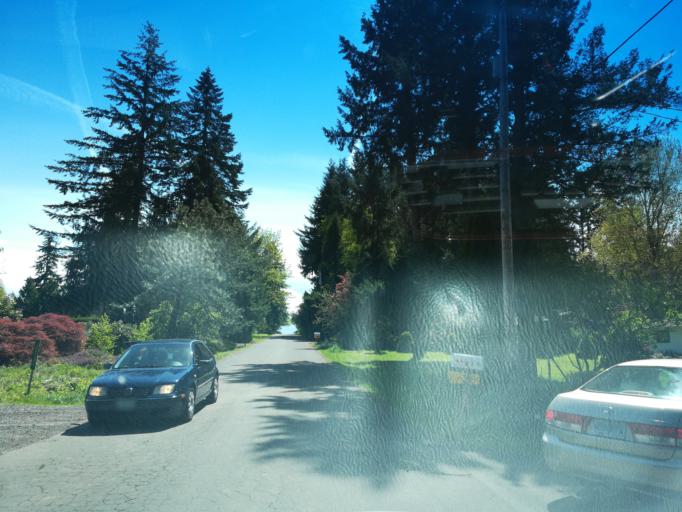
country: US
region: Oregon
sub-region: Clackamas County
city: Damascus
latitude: 45.4355
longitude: -122.4178
